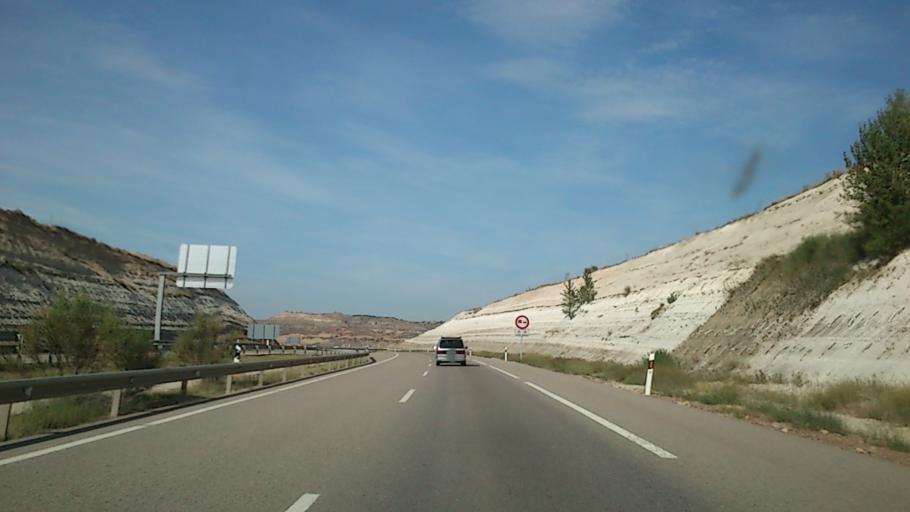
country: ES
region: Aragon
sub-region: Provincia de Teruel
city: Calamocha
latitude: 40.9185
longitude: -1.2701
